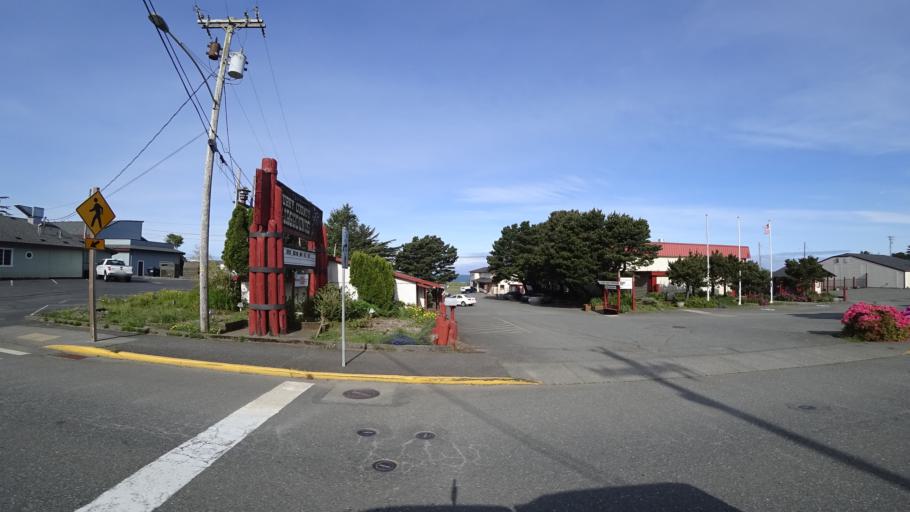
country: US
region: Oregon
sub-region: Curry County
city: Gold Beach
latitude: 42.4053
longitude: -124.4213
